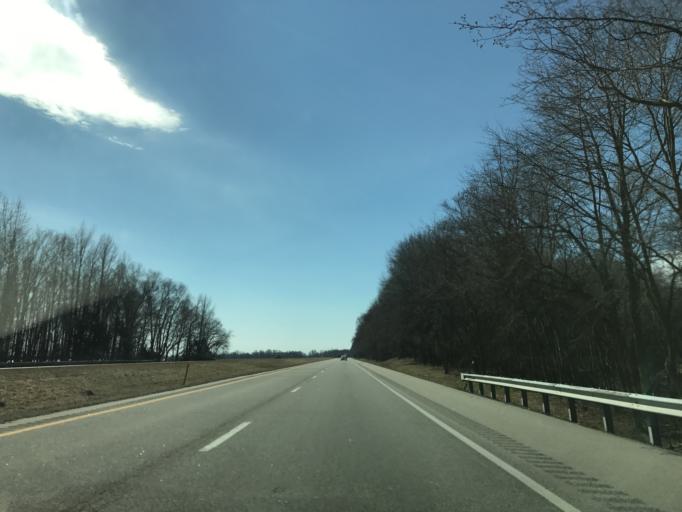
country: US
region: Maryland
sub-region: Queen Anne's County
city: Kingstown
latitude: 39.1298
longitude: -75.9364
